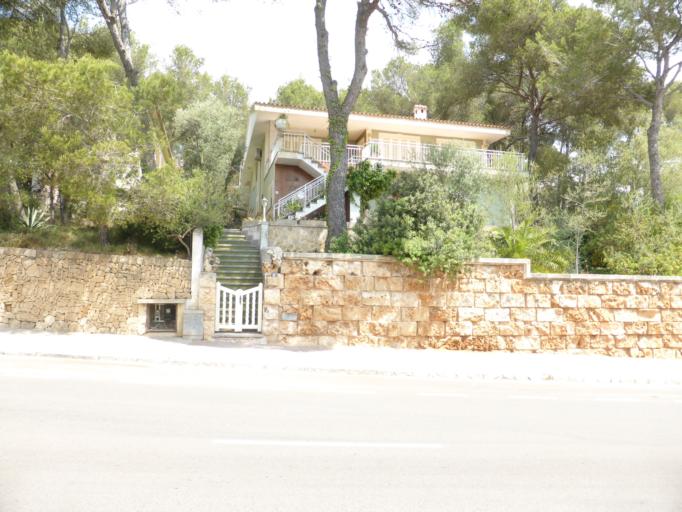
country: ES
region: Balearic Islands
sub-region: Illes Balears
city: Port d'Alcudia
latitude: 39.8364
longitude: 3.1495
